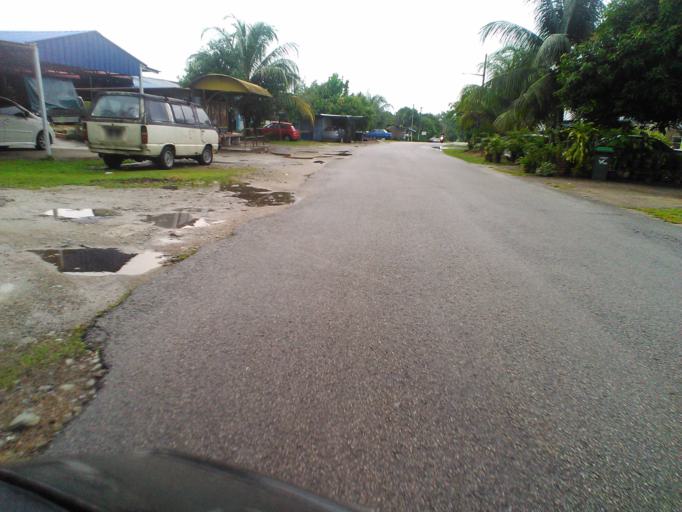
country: MY
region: Kedah
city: Kulim
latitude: 5.3661
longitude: 100.5681
